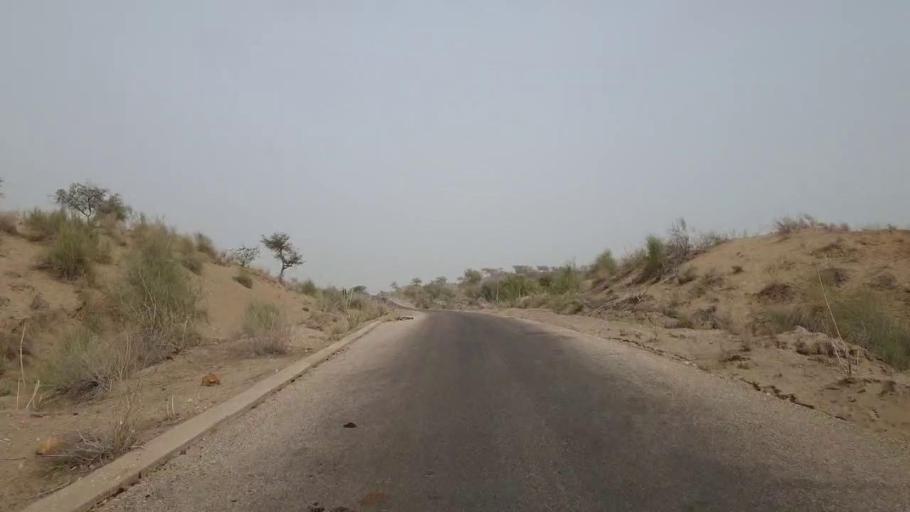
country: PK
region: Sindh
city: Islamkot
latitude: 24.5879
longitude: 70.2918
